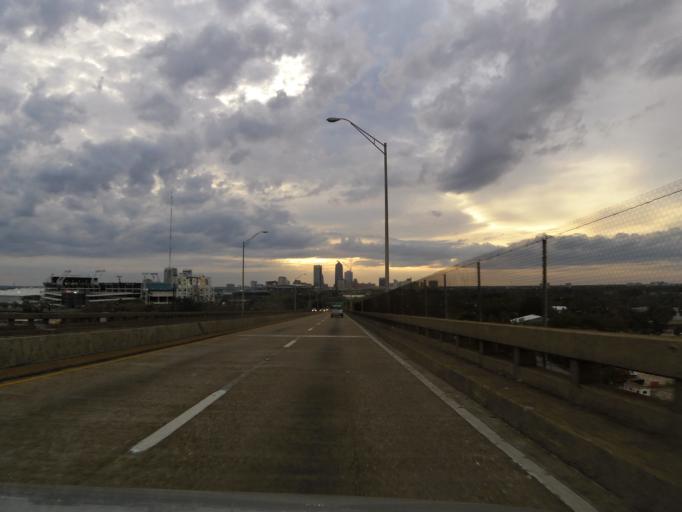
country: US
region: Florida
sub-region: Duval County
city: Jacksonville
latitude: 30.3274
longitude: -81.6288
